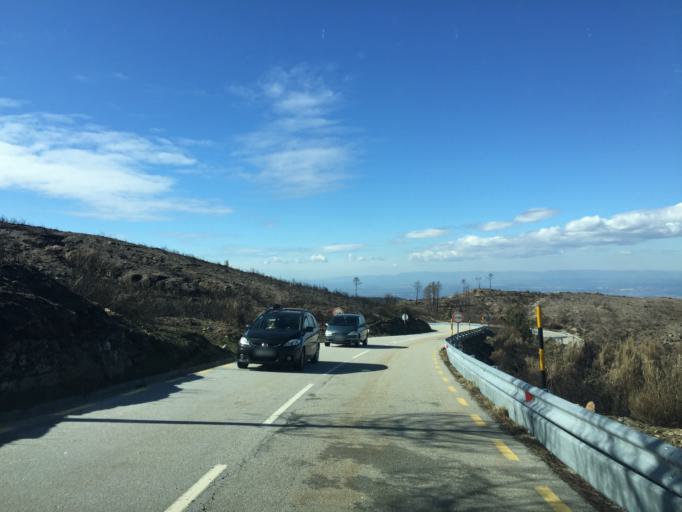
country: PT
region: Guarda
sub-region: Seia
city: Seia
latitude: 40.3951
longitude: -7.6513
